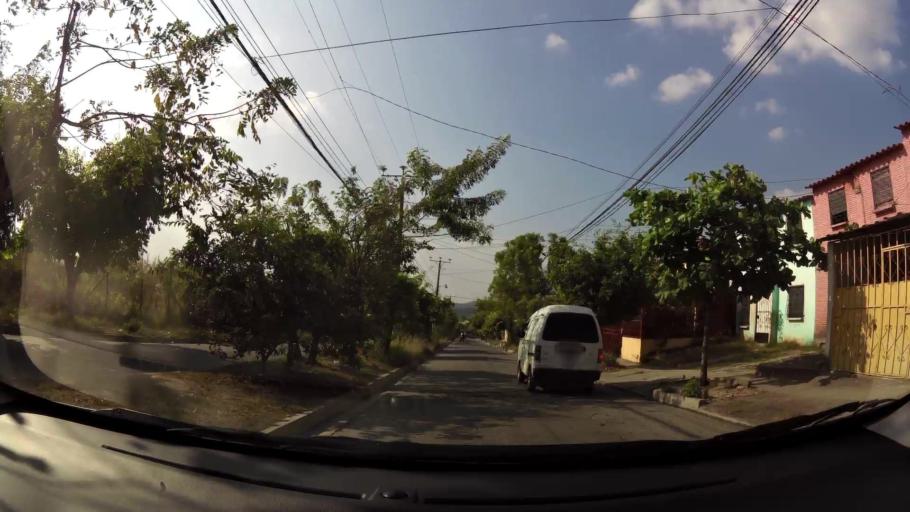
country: SV
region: San Salvador
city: Ilopango
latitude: 13.7234
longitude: -89.1070
